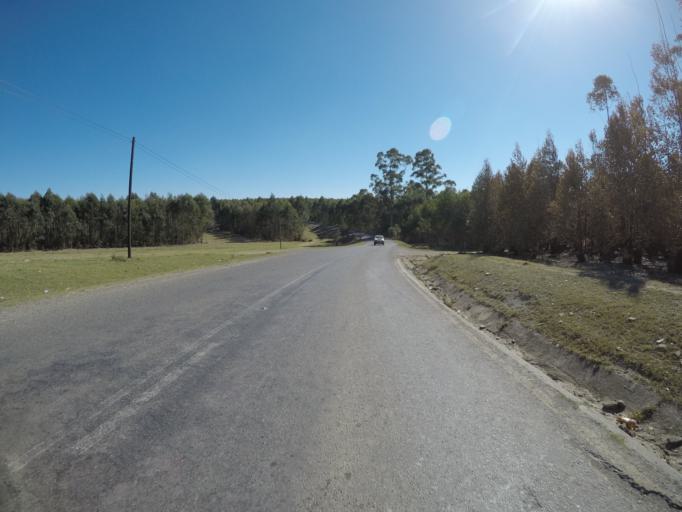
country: ZA
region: Eastern Cape
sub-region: OR Tambo District Municipality
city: Mthatha
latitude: -31.7773
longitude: 28.7373
